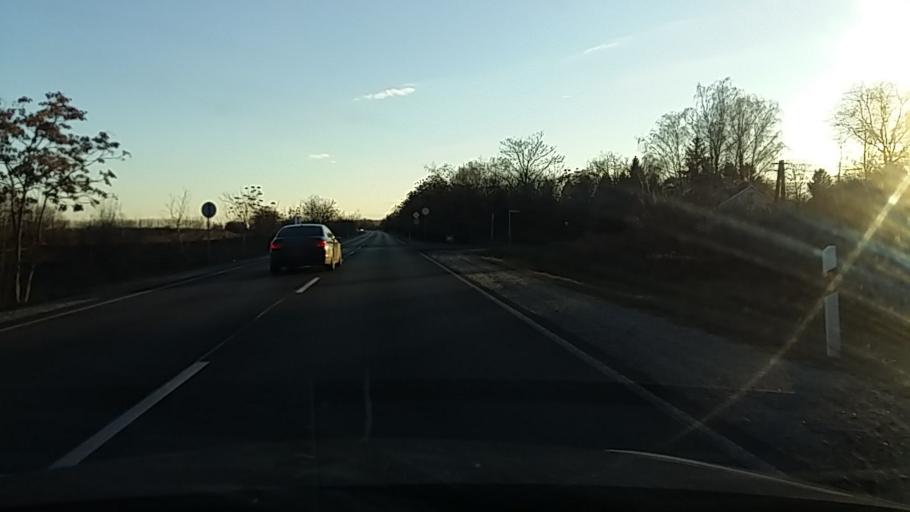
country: HU
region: Szabolcs-Szatmar-Bereg
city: Ujfeherto
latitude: 47.8599
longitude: 21.7043
